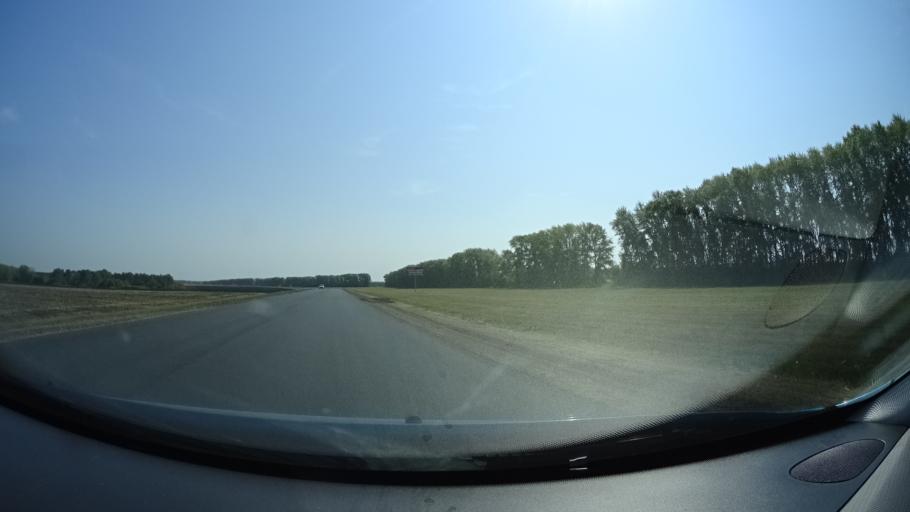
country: RU
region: Bashkortostan
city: Karmaskaly
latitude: 54.3881
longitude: 56.1313
